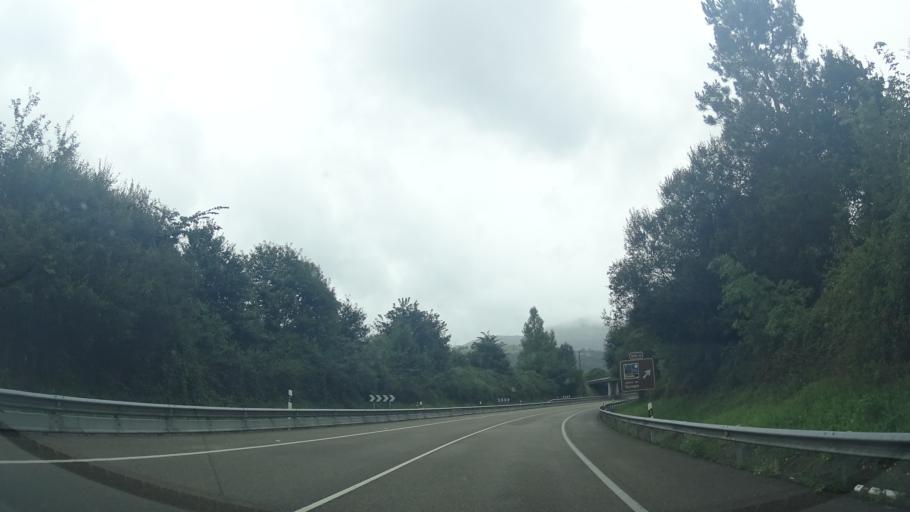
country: ES
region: Asturias
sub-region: Province of Asturias
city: Parres
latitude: 43.3817
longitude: -5.1816
